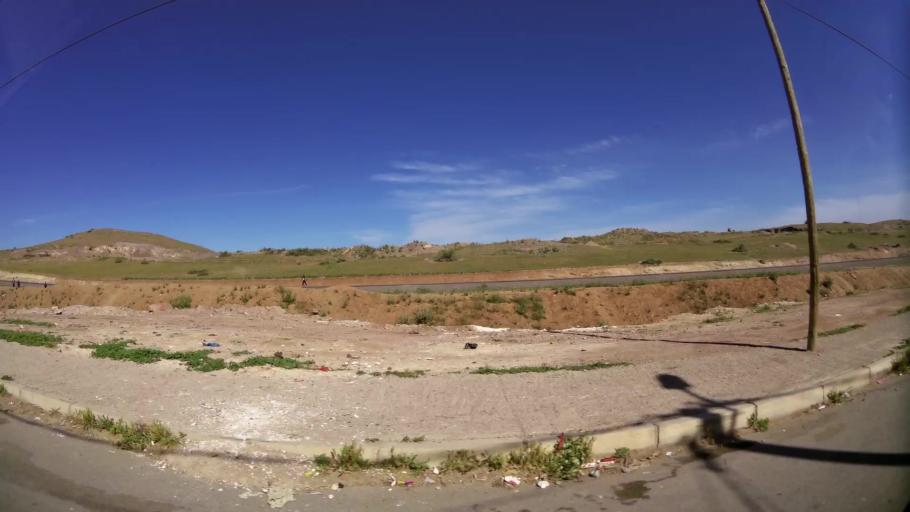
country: MA
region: Oriental
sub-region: Oujda-Angad
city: Oujda
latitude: 34.6452
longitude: -1.9504
